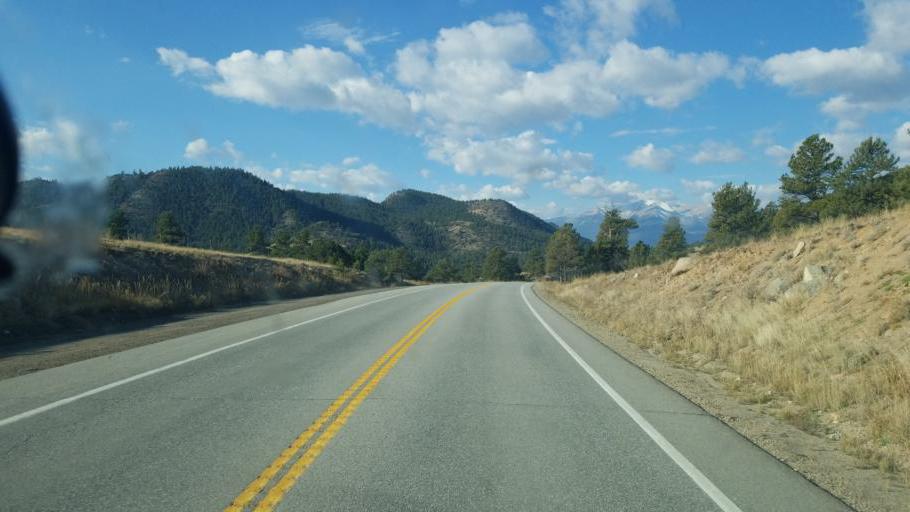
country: US
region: Colorado
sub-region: Chaffee County
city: Buena Vista
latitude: 38.8436
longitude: -105.9916
